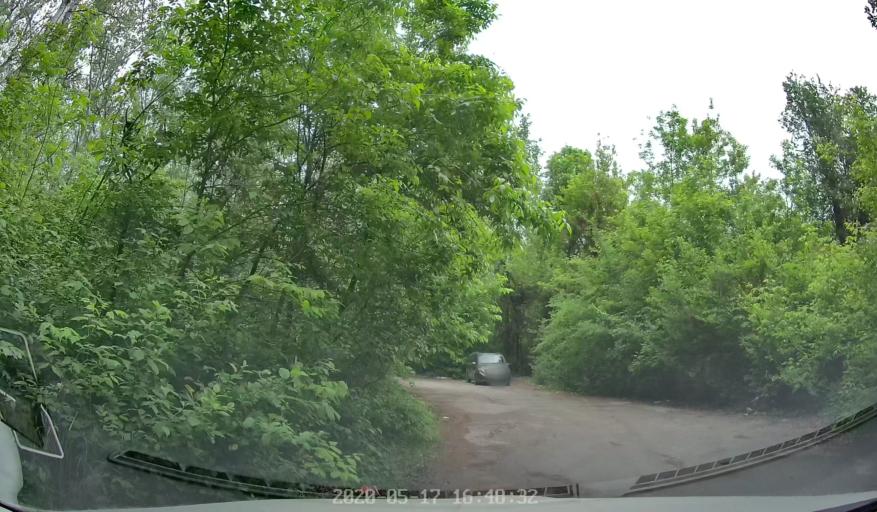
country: MD
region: Chisinau
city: Vatra
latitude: 47.0509
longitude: 28.7886
